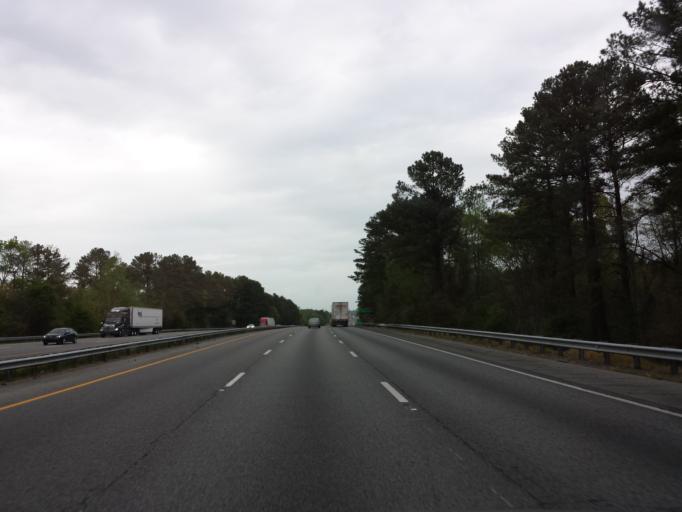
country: US
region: Georgia
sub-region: Houston County
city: Perry
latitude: 32.4127
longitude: -83.7629
